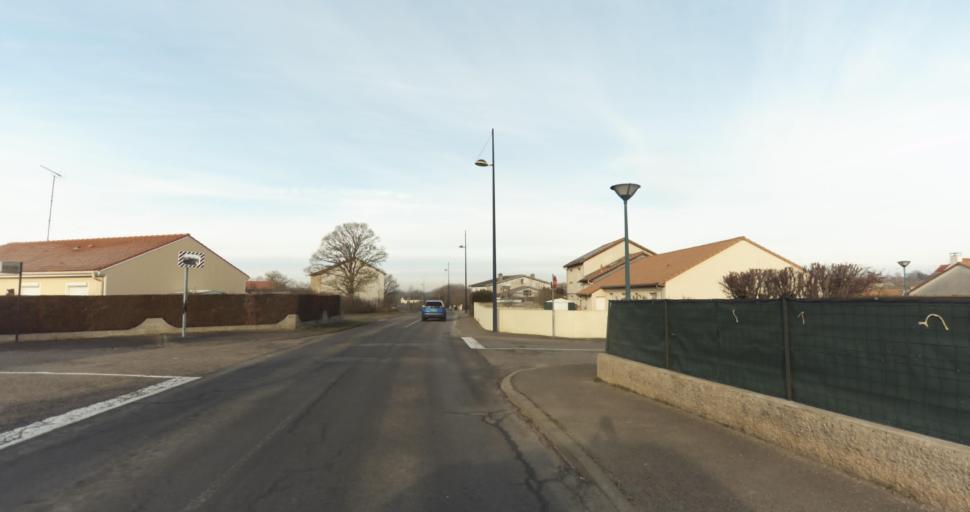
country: FR
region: Lorraine
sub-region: Departement de Meurthe-et-Moselle
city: Labry
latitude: 49.1663
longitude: 5.8868
